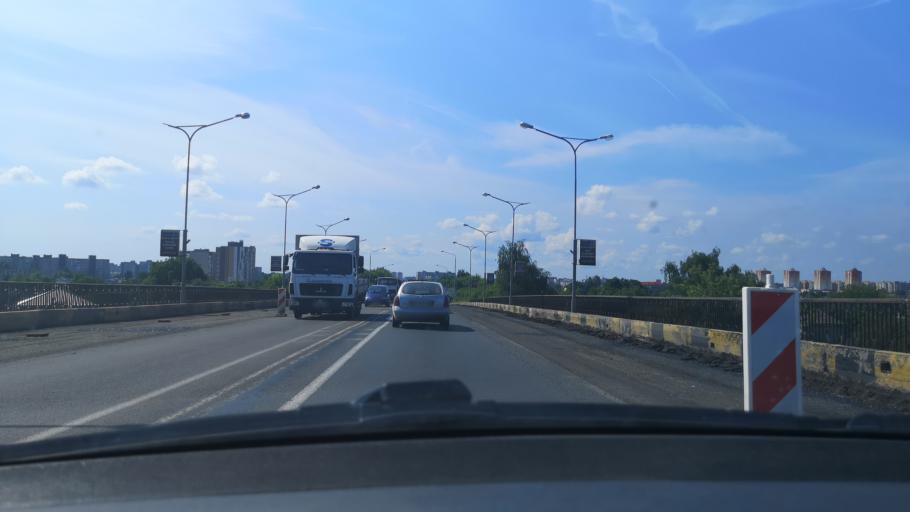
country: BY
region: Brest
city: Brest
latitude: 52.1076
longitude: 23.7176
